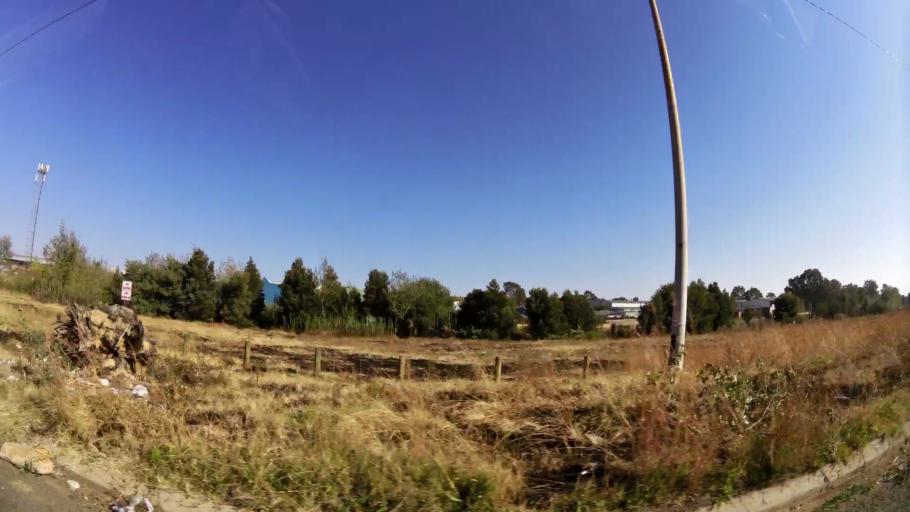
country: ZA
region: Gauteng
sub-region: City of Johannesburg Metropolitan Municipality
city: Modderfontein
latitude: -26.0632
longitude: 28.1978
